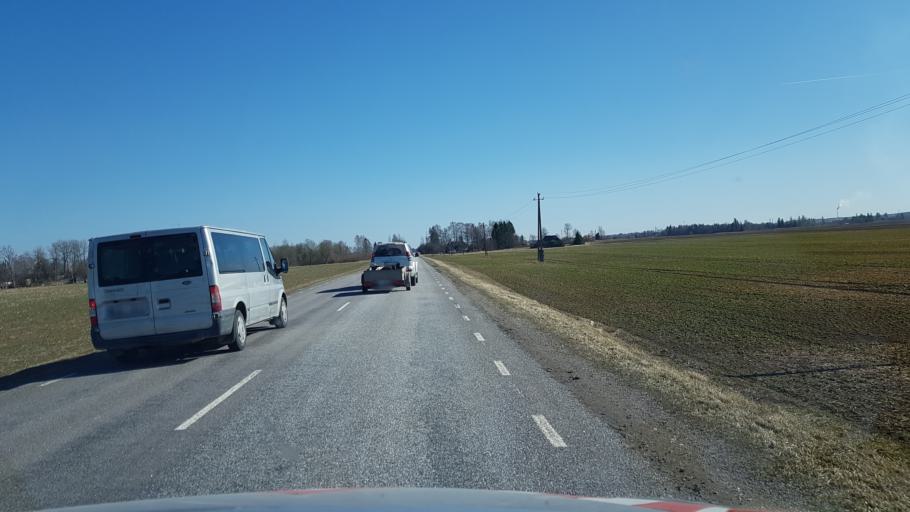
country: EE
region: Laeaene-Virumaa
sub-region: Vaeike-Maarja vald
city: Vaike-Maarja
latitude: 59.1494
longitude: 26.2244
